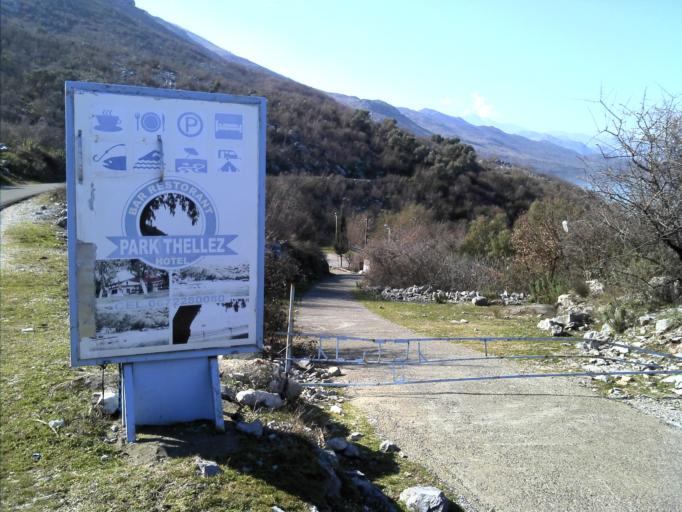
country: AL
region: Shkoder
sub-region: Rrethi i Shkodres
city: Dajc
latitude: 42.0687
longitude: 19.4155
